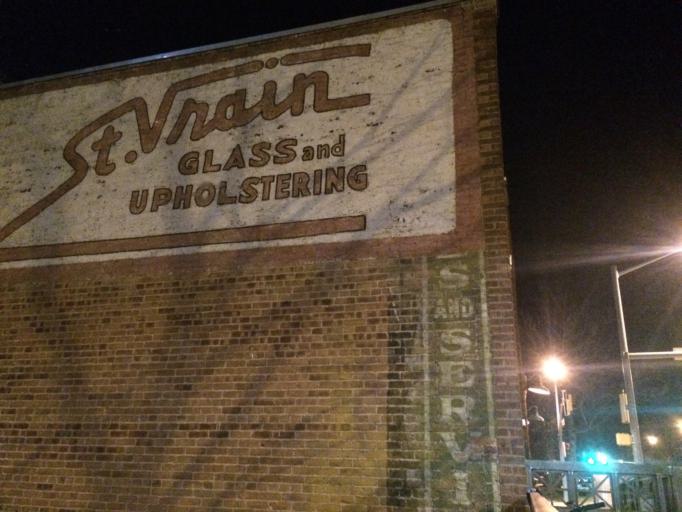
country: US
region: Colorado
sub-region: Boulder County
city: Longmont
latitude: 40.1638
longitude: -105.1034
